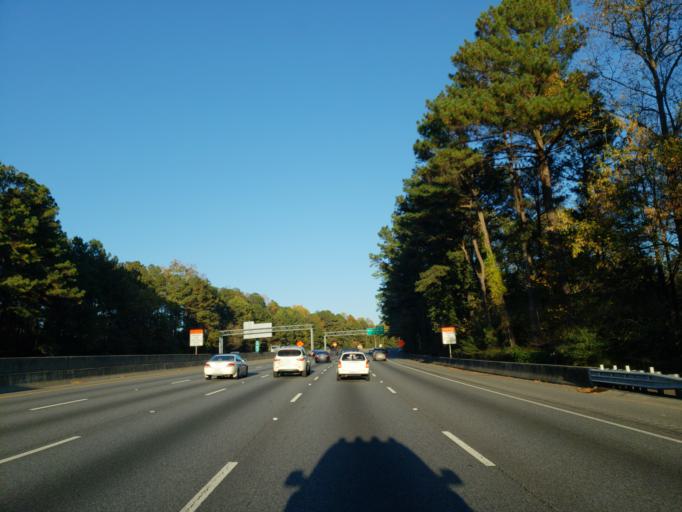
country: US
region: Georgia
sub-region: Cobb County
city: Fair Oaks
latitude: 33.9024
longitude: -84.5406
